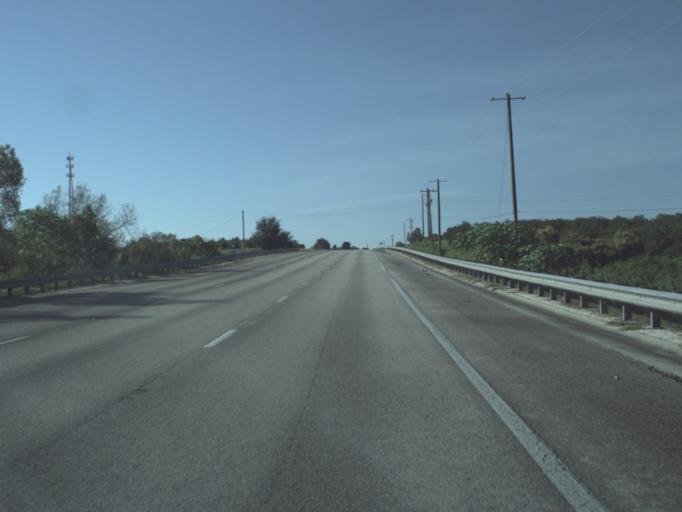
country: US
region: Florida
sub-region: Hardee County
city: Wauchula
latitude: 27.5246
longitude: -81.8093
